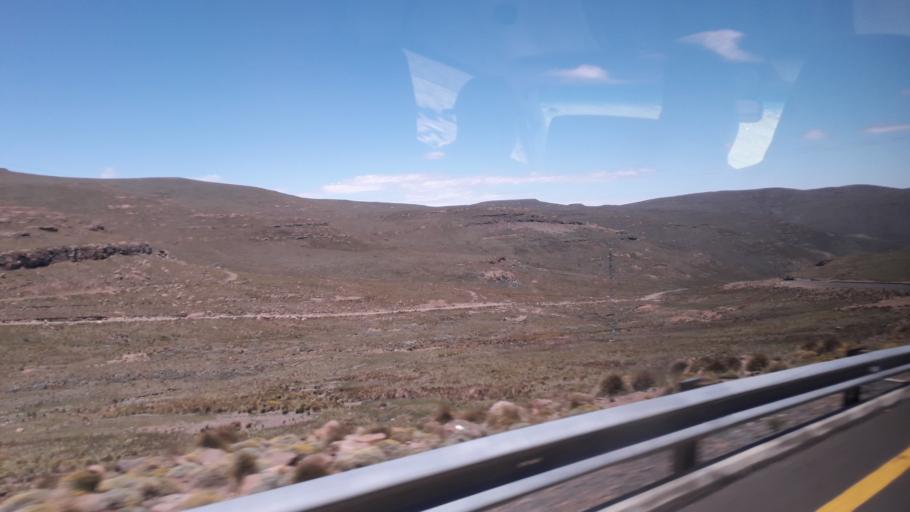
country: ZA
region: Orange Free State
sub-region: Thabo Mofutsanyana District Municipality
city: Phuthaditjhaba
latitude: -28.8097
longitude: 28.7104
